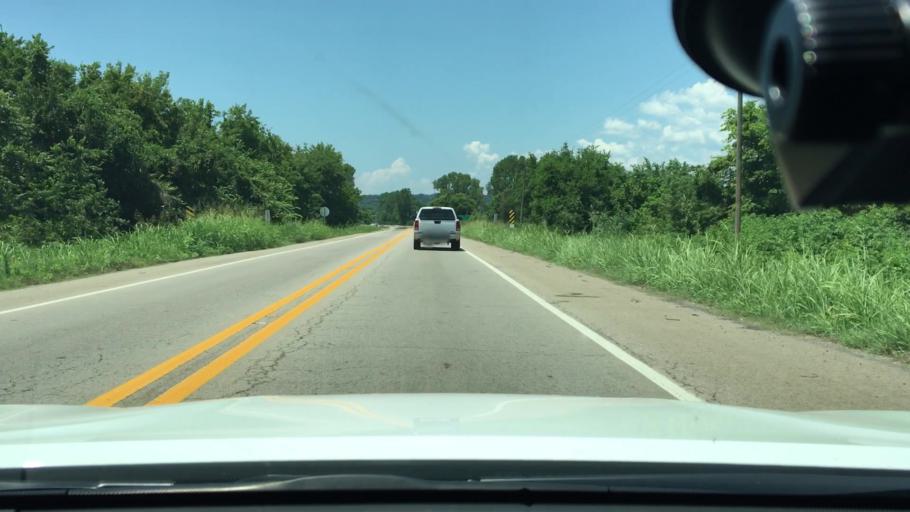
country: US
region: Arkansas
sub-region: Crawford County
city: Van Buren
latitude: 35.4195
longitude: -94.3361
